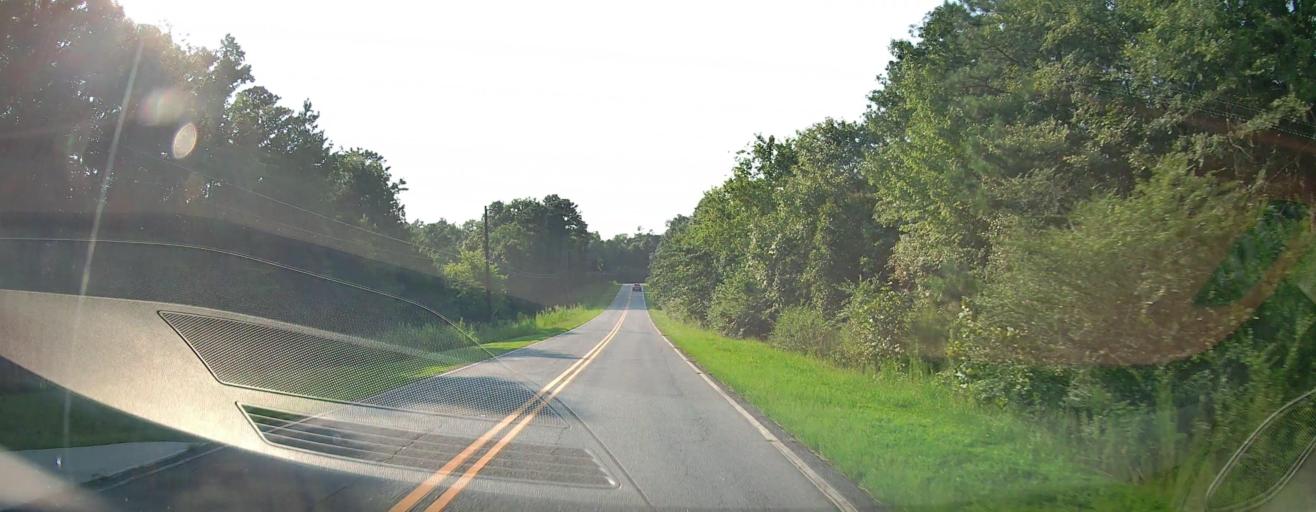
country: US
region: Georgia
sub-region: Bibb County
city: West Point
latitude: 32.8345
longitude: -83.8084
